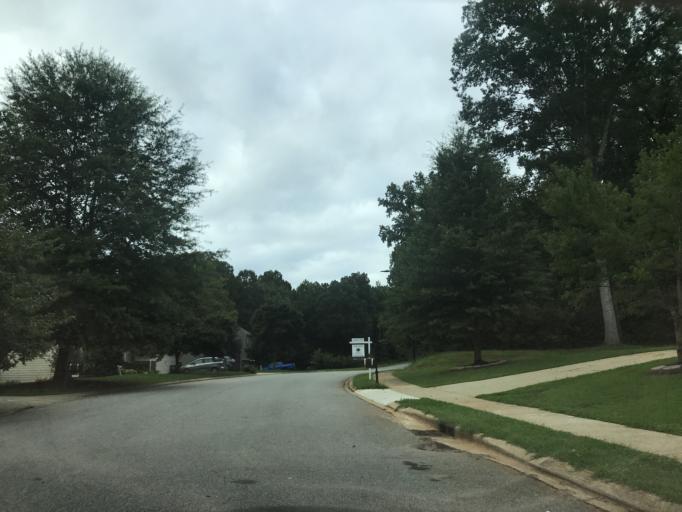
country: US
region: North Carolina
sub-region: Wake County
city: Garner
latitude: 35.5797
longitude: -78.5834
